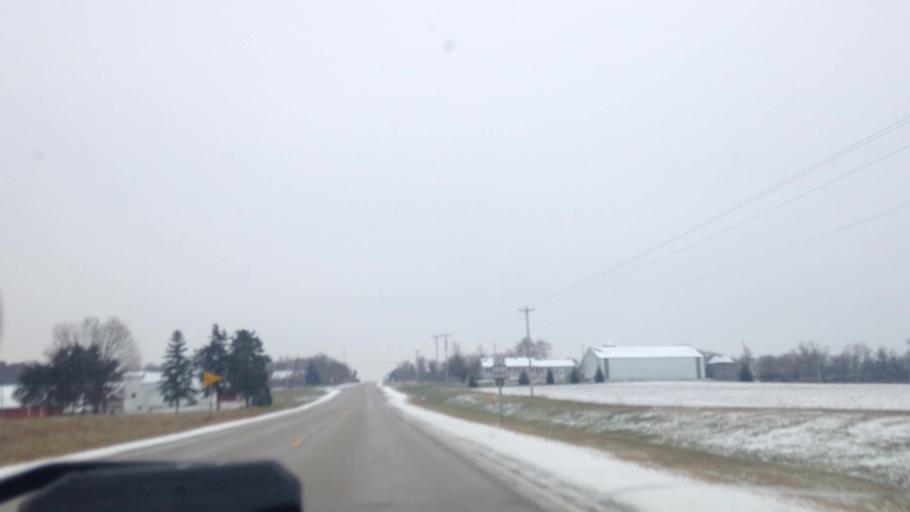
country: US
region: Wisconsin
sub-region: Dodge County
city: Hustisford
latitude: 43.2707
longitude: -88.5181
